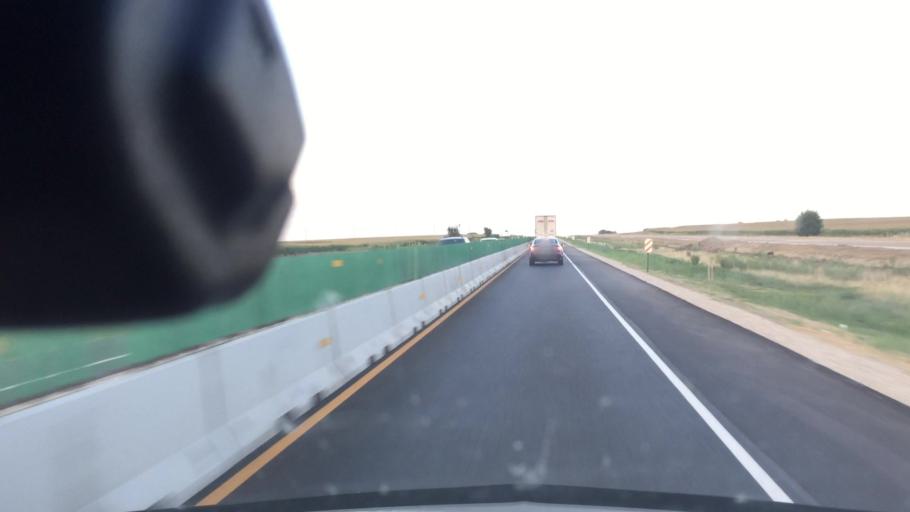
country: US
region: Illinois
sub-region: Livingston County
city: Pontiac
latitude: 40.9309
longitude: -88.6167
